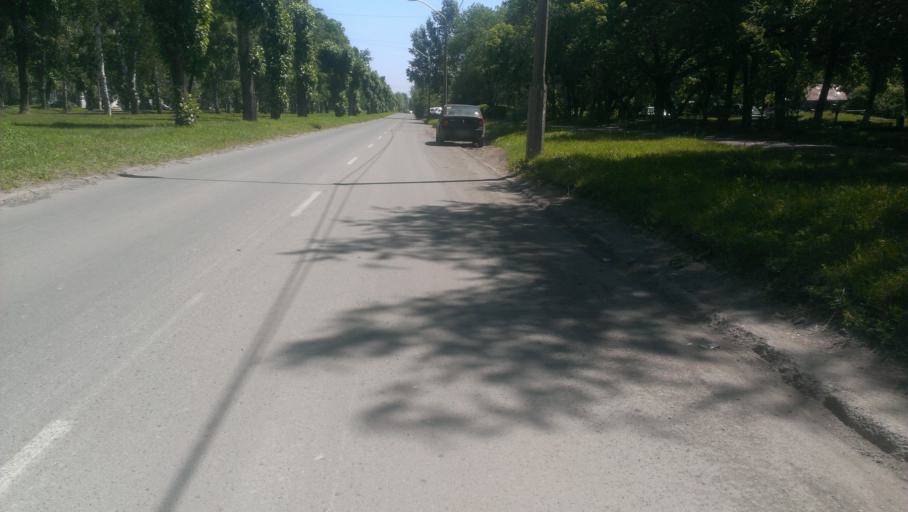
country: RU
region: Altai Krai
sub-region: Gorod Barnaulskiy
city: Barnaul
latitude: 53.3623
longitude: 83.7084
